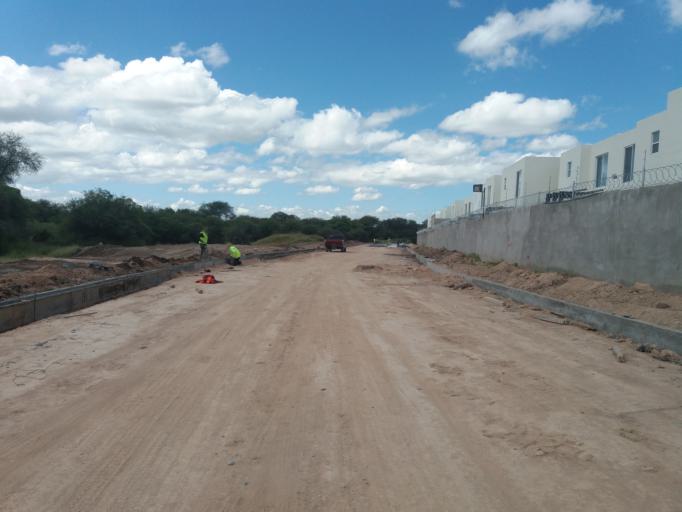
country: MX
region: Aguascalientes
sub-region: Aguascalientes
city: San Sebastian [Fraccionamiento]
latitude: 21.8186
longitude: -102.2724
